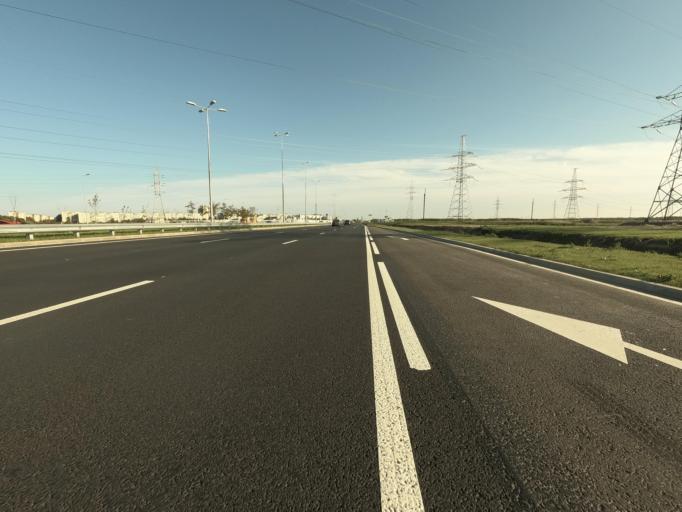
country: RU
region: St.-Petersburg
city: Kolpino
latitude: 59.7416
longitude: 30.5451
